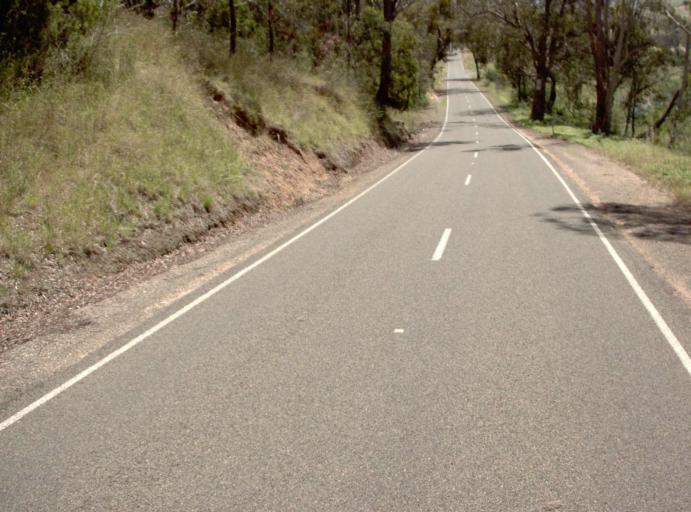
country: AU
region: Victoria
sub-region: East Gippsland
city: Bairnsdale
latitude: -37.4124
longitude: 147.8346
